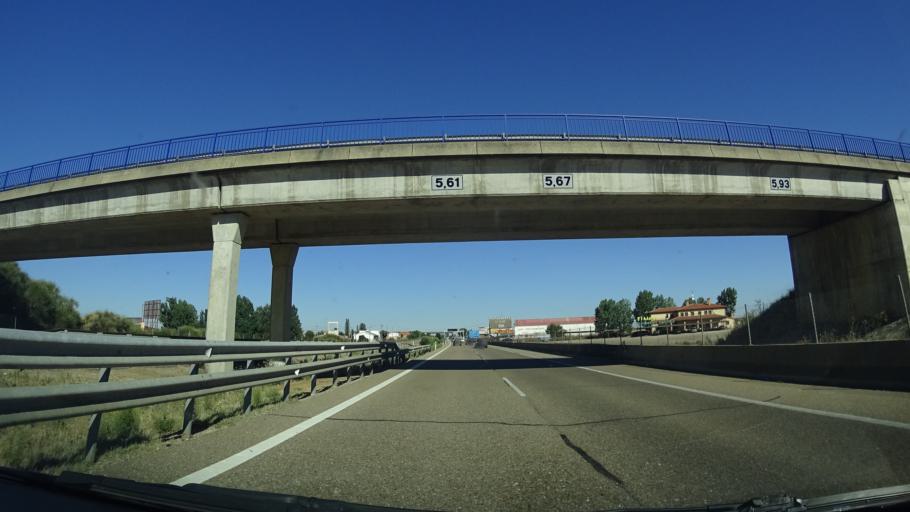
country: ES
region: Castille and Leon
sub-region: Provincia de Zamora
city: San Esteban del Molar
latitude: 41.9373
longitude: -5.5452
